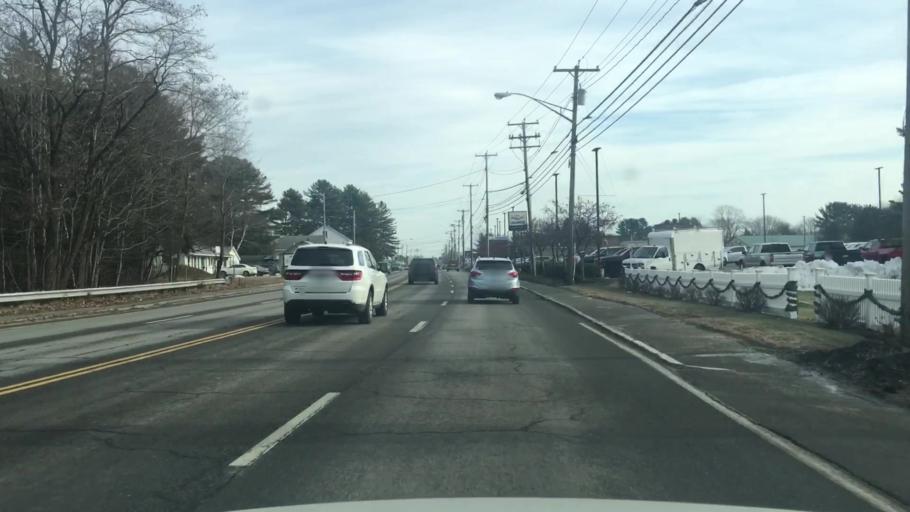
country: US
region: Maine
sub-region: Sagadahoc County
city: Topsham
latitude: 43.9120
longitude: -69.9943
